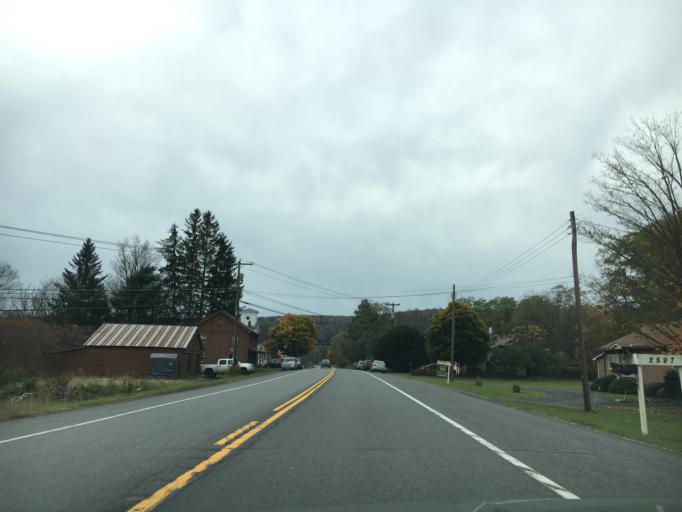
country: US
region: New York
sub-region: Otsego County
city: Oneonta
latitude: 42.5255
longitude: -74.9879
